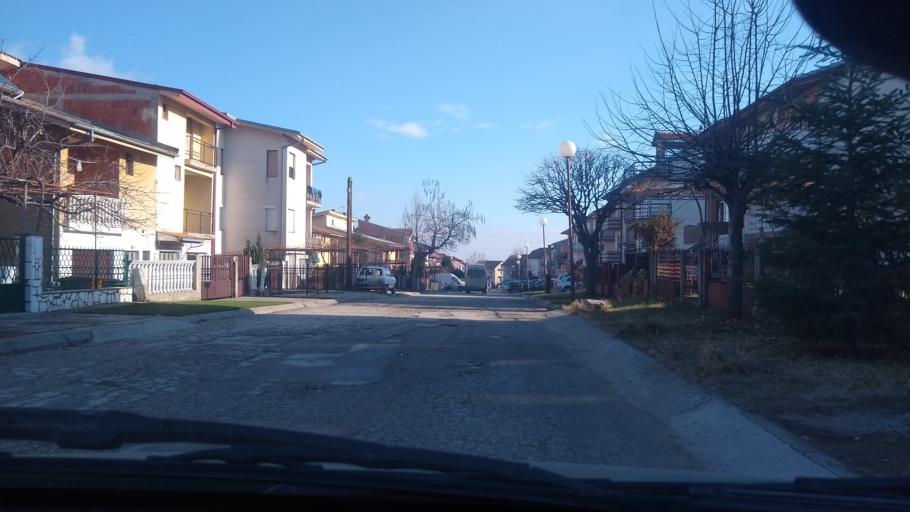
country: MK
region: Bitola
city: Bitola
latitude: 41.0044
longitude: 21.3441
